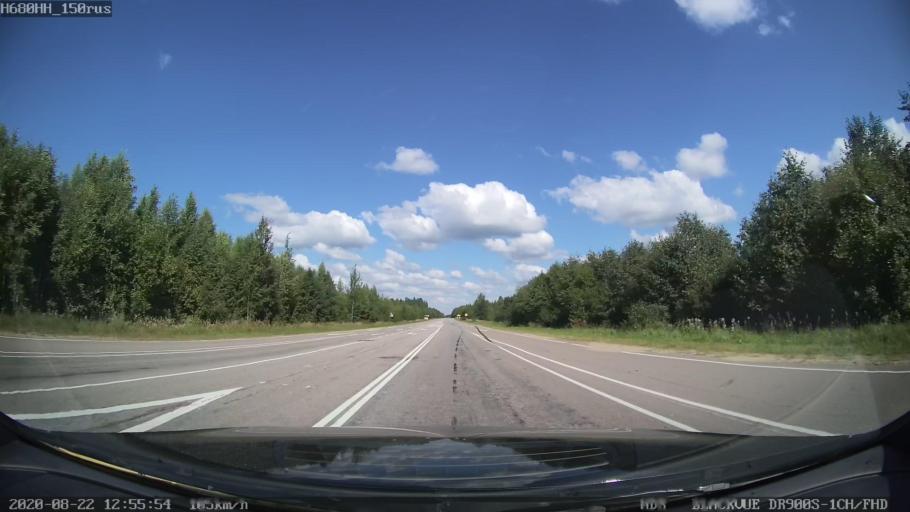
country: RU
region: Tverskaya
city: Rameshki
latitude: 57.5487
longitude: 36.3100
